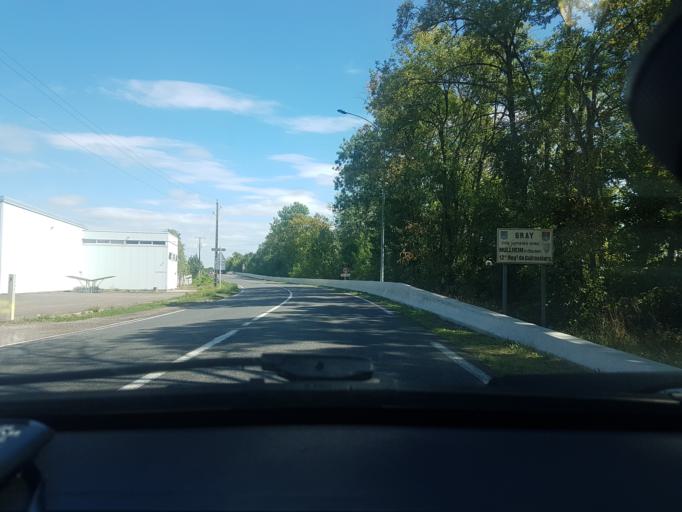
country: FR
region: Franche-Comte
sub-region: Departement de la Haute-Saone
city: Gray-la-Ville
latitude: 47.4487
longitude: 5.5722
